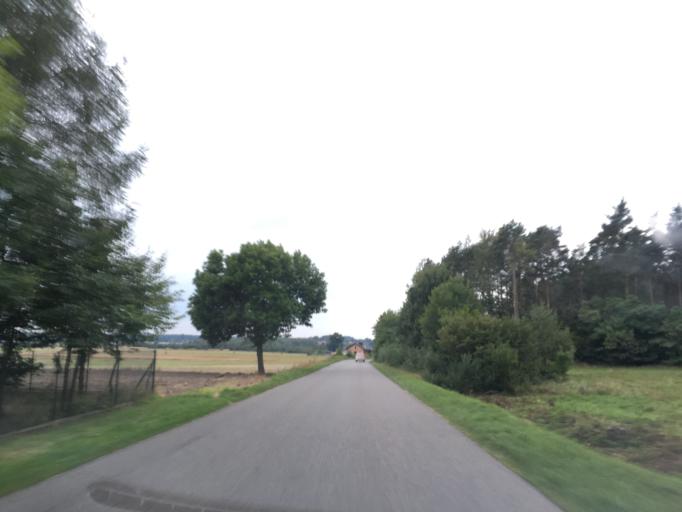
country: PL
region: Lodz Voivodeship
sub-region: Powiat piotrkowski
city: Reczno
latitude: 51.1905
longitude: 19.8307
